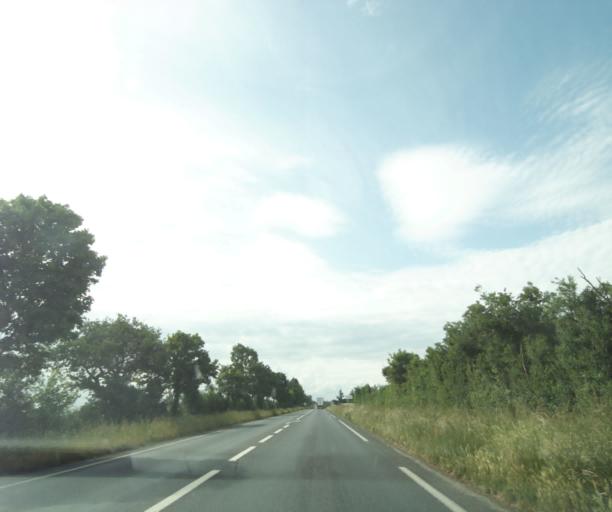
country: FR
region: Pays de la Loire
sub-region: Departement de la Sarthe
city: Solesmes
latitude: 47.8190
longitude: -0.2948
